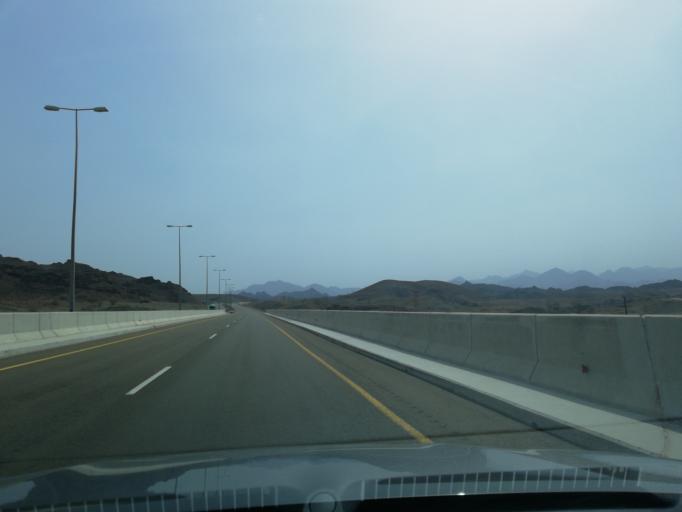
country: OM
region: Al Batinah
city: Al Liwa'
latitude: 24.2862
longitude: 56.4143
